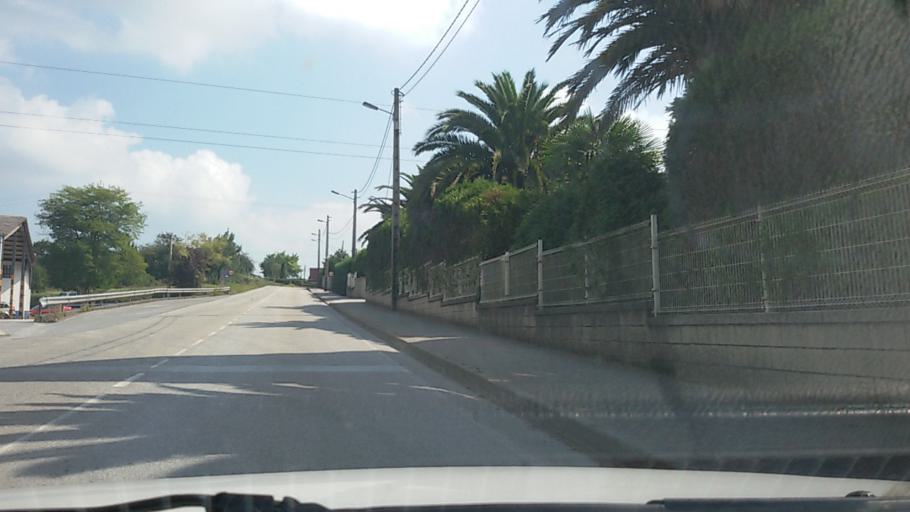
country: ES
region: Asturias
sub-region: Province of Asturias
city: Lugones
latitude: 43.4406
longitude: -5.8125
